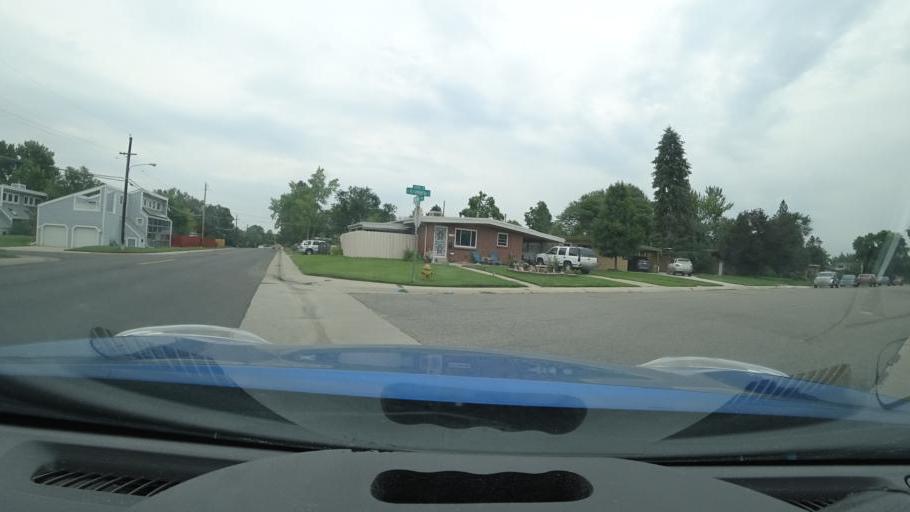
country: US
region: Colorado
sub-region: Arapahoe County
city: Glendale
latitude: 39.6894
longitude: -104.9164
